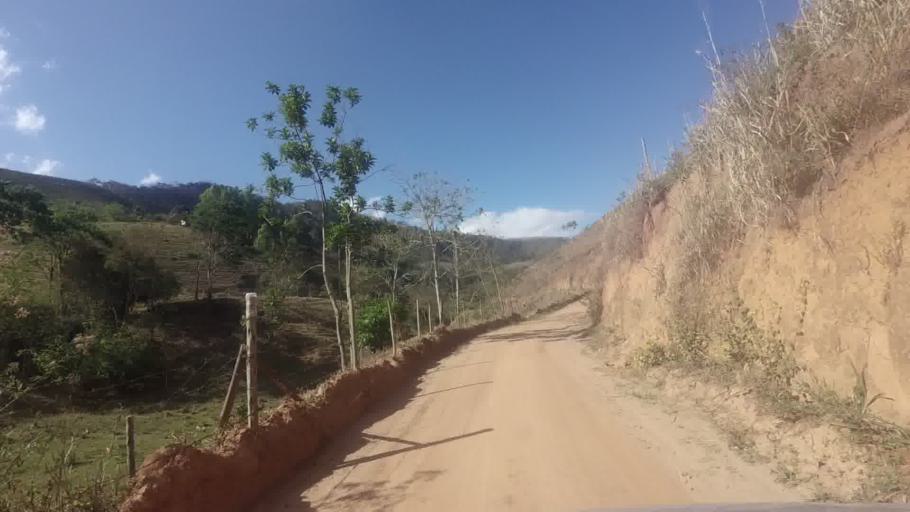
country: BR
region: Espirito Santo
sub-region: Sao Jose Do Calcado
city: Sao Jose do Calcado
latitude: -21.0353
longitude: -41.5991
